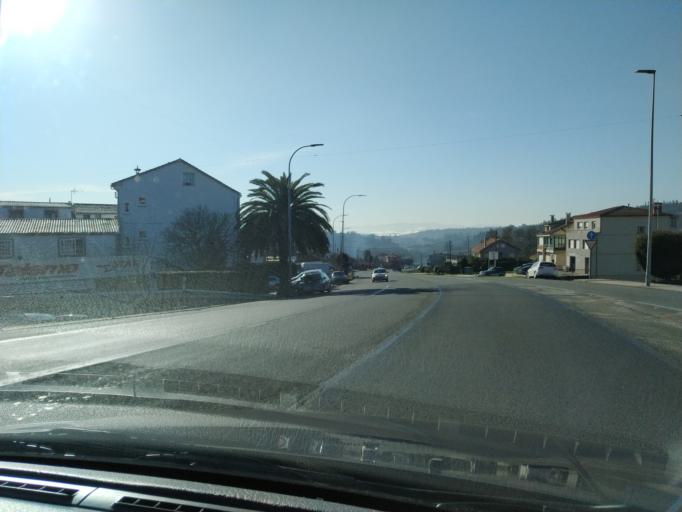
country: ES
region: Galicia
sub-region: Provincia da Coruna
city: Santiago de Compostela
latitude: 42.8494
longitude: -8.5253
